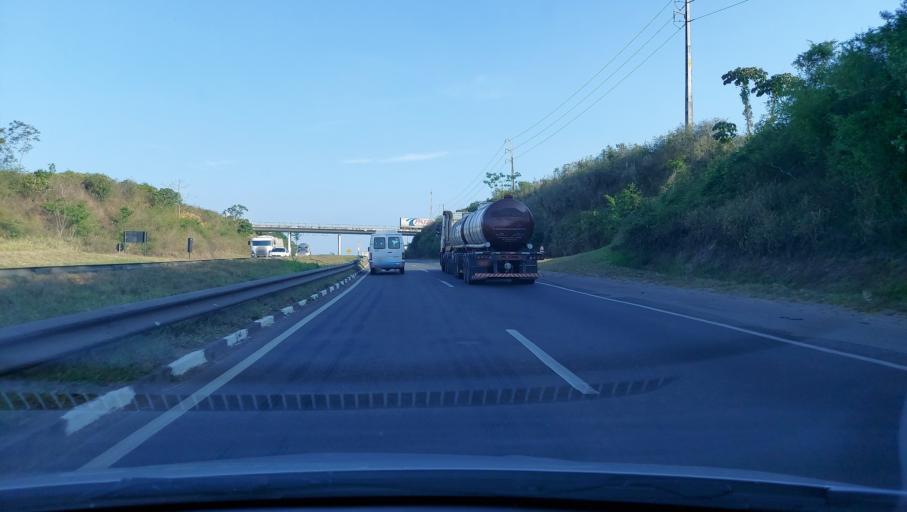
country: BR
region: Bahia
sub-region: Conceicao Do Jacuipe
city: Conceicao do Jacuipe
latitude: -12.3589
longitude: -38.8269
